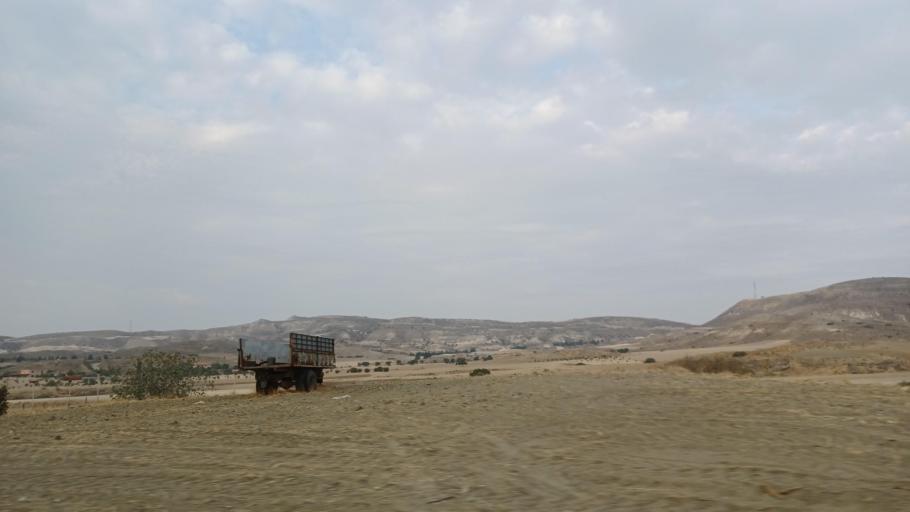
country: CY
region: Larnaka
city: Troulloi
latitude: 35.0139
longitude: 33.5725
